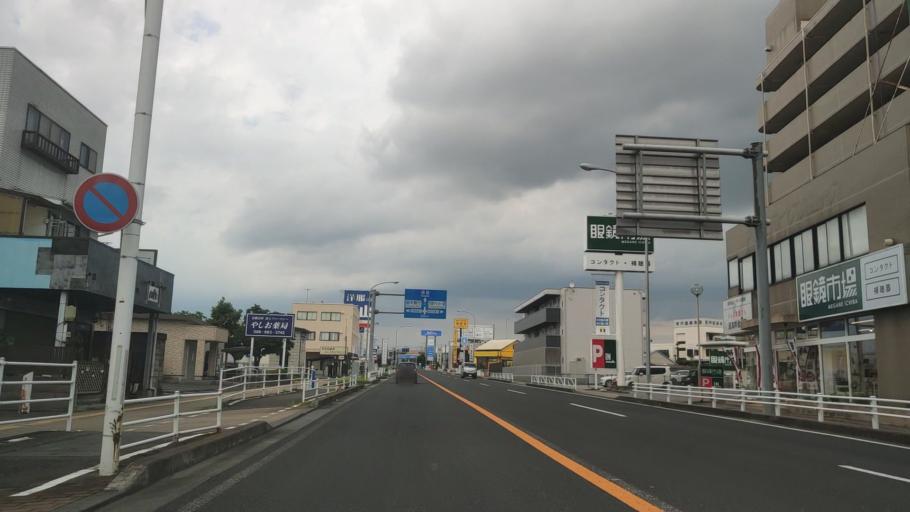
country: JP
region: Tochigi
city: Utsunomiya-shi
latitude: 36.5600
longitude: 139.9141
